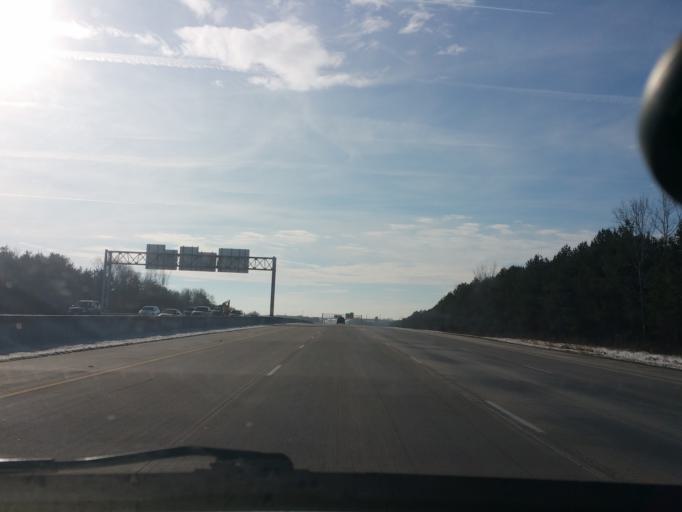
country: US
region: Iowa
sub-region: Polk County
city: Clive
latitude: 41.5827
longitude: -93.7778
